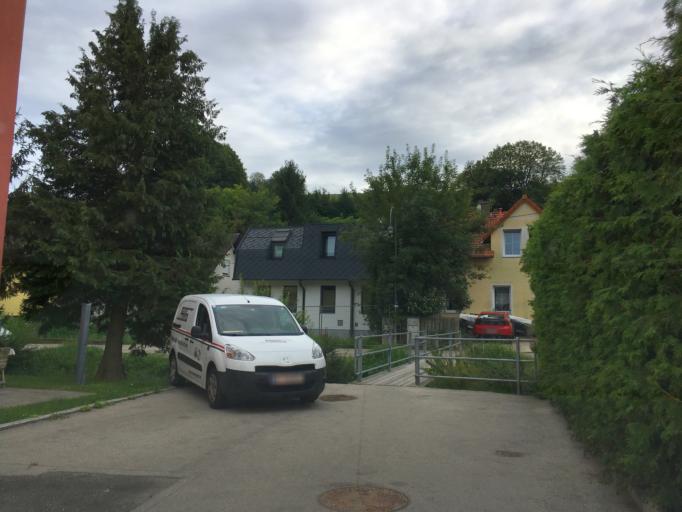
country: AT
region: Lower Austria
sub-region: Politischer Bezirk Tulln
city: Wordern
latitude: 48.3119
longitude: 16.2501
